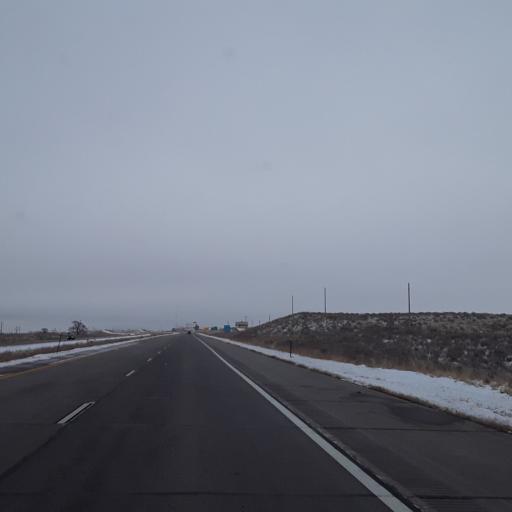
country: US
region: Colorado
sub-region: Logan County
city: Sterling
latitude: 40.6063
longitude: -103.1808
